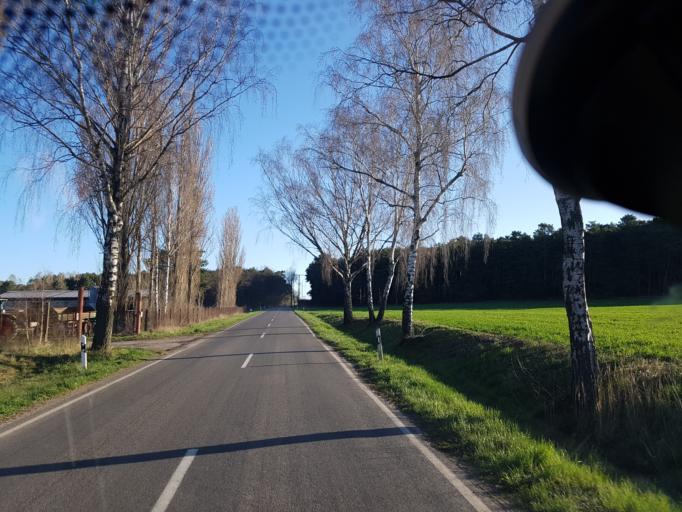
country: DE
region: Brandenburg
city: Jamlitz
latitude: 52.0492
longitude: 14.4250
